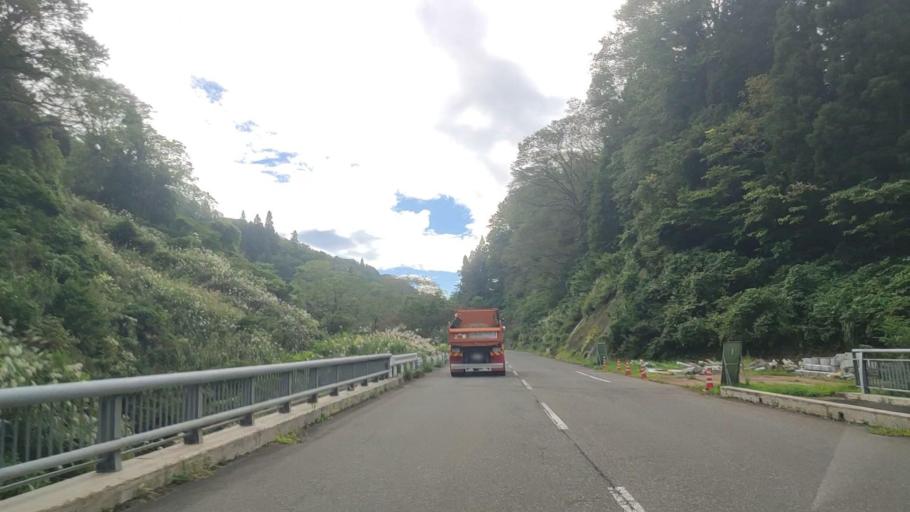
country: JP
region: Nagano
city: Iiyama
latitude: 36.8990
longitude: 138.3190
